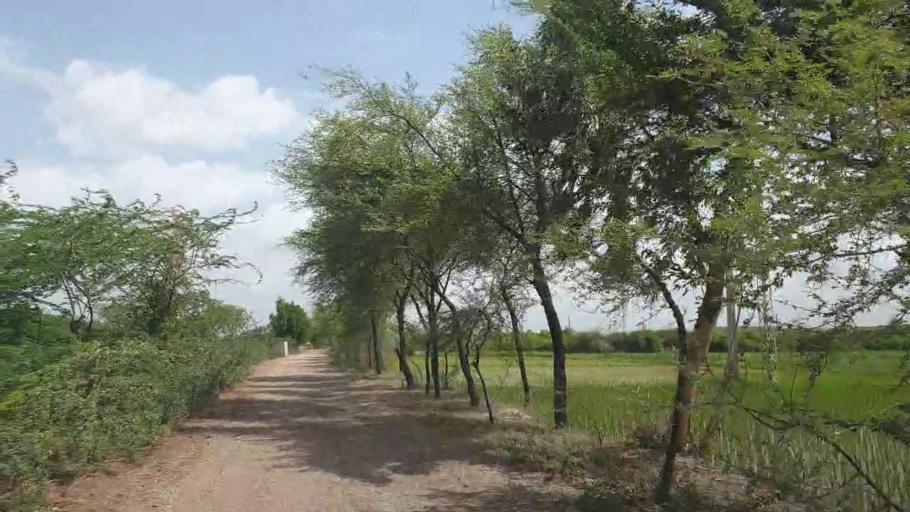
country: PK
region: Sindh
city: Tando Bago
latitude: 24.6508
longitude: 68.9931
